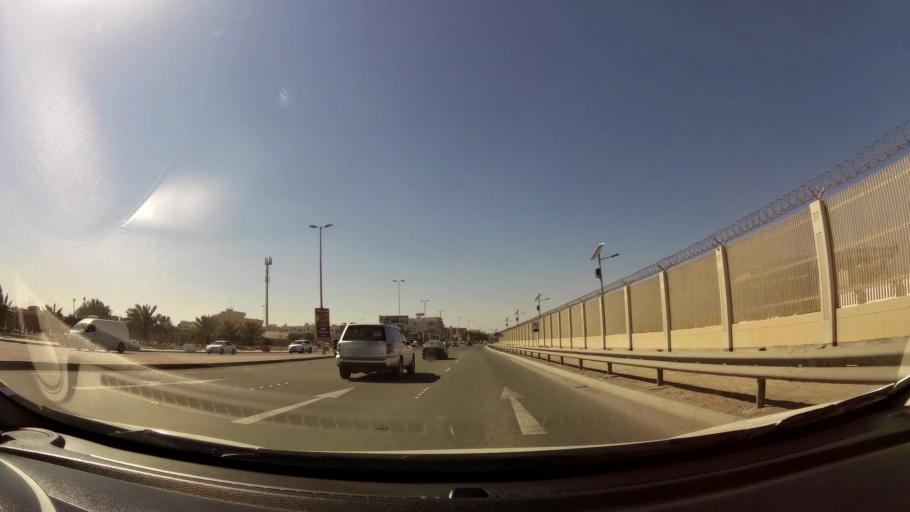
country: BH
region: Muharraq
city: Al Hadd
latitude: 26.2569
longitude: 50.6506
